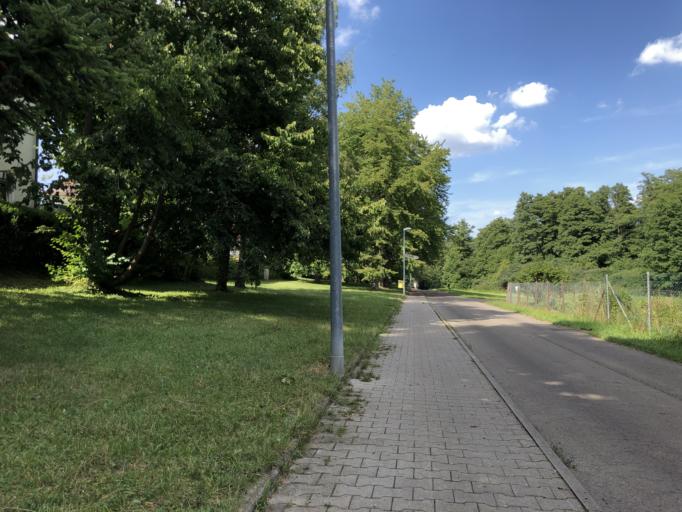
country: DE
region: Baden-Wuerttemberg
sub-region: Regierungsbezirk Stuttgart
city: Sindelfingen
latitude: 48.7217
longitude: 9.0145
